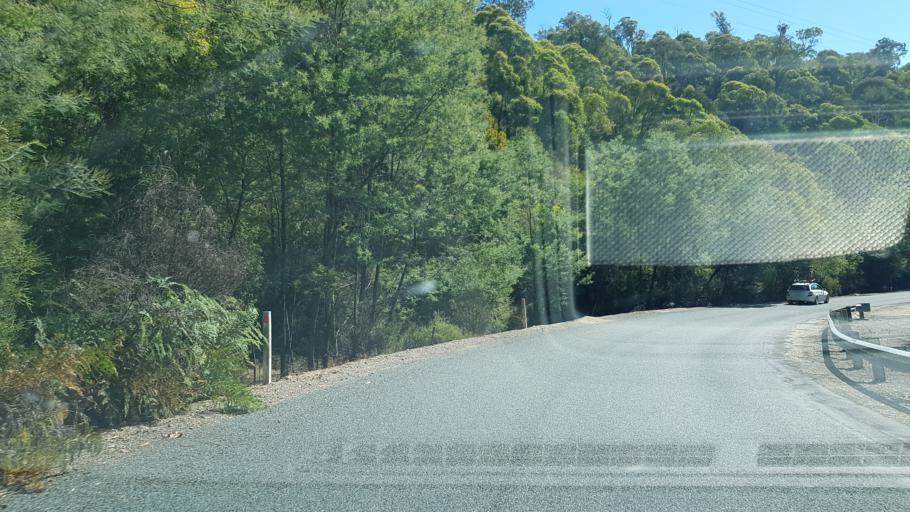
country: AU
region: Victoria
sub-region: Mansfield
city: Mansfield
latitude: -36.9055
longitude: 146.3918
